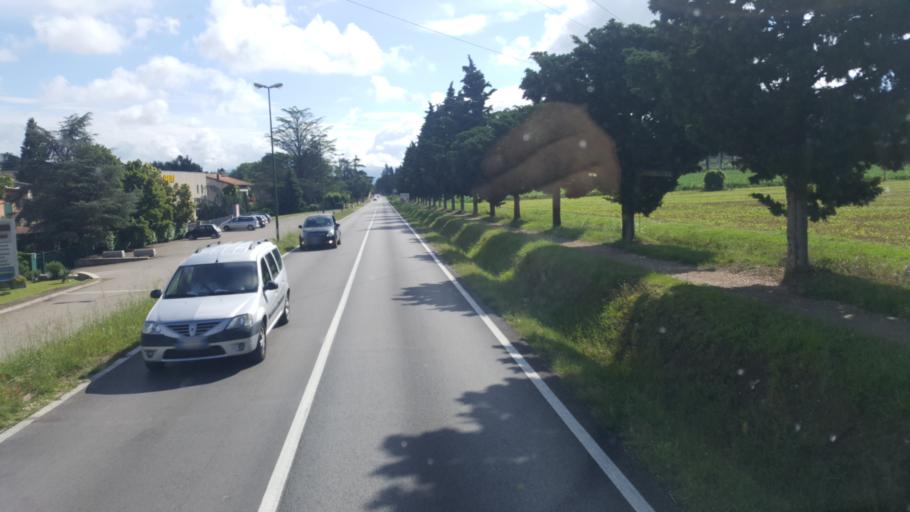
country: IT
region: Umbria
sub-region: Provincia di Perugia
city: Torgiano
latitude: 43.0211
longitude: 12.4411
